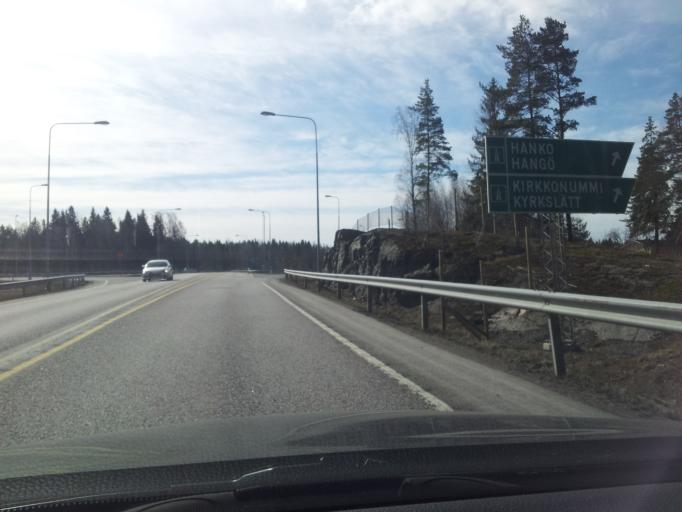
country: FI
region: Uusimaa
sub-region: Helsinki
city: Kirkkonummi
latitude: 60.1393
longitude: 24.5349
